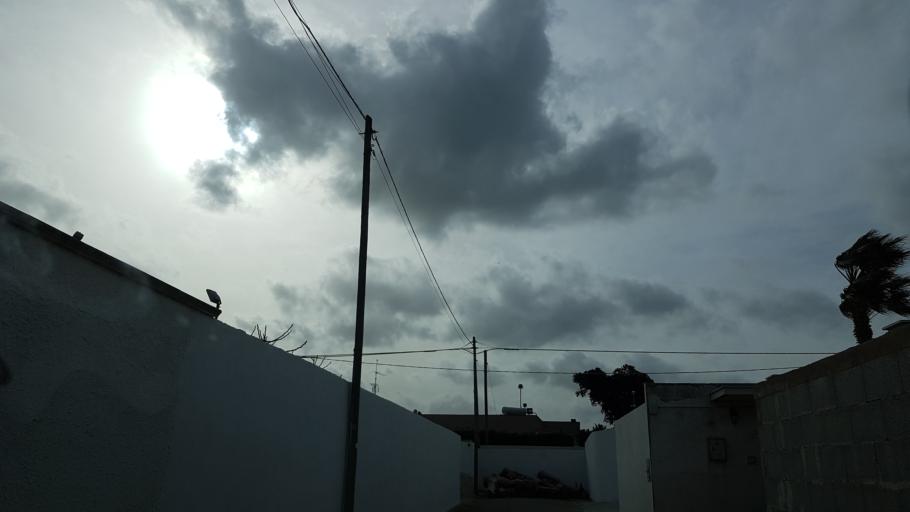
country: IT
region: Apulia
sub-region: Provincia di Brindisi
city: Materdomini
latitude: 40.6742
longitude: 17.9419
